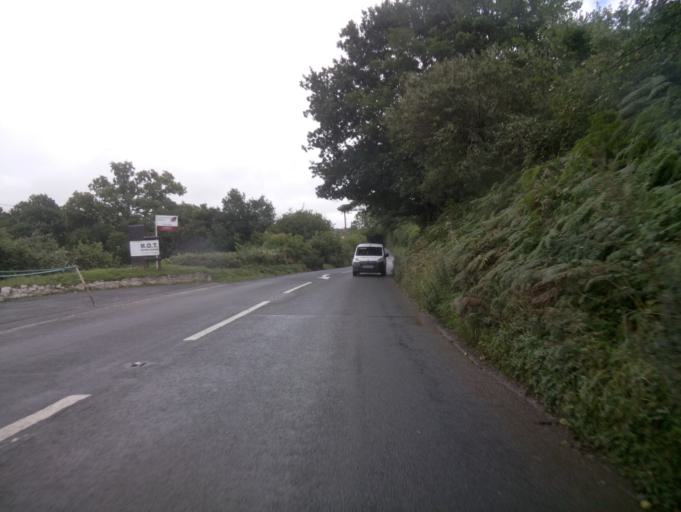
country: GB
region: England
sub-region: Devon
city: Modbury
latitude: 50.3341
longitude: -3.8507
